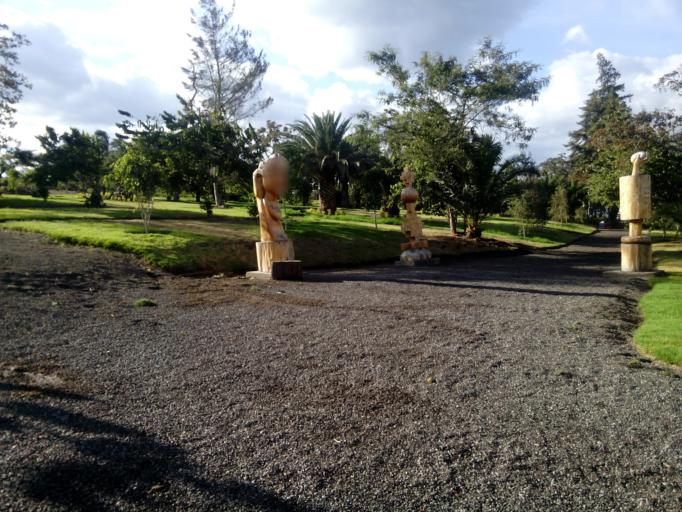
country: EC
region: Imbabura
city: Ibarra
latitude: 0.4053
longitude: -78.1759
